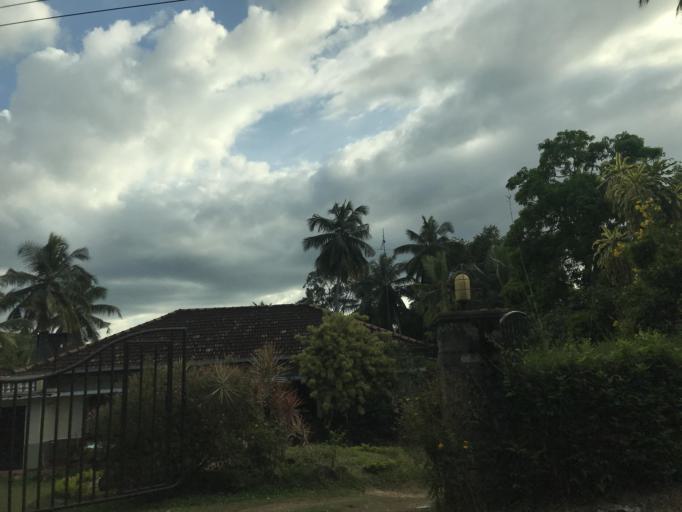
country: LK
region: Western
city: Gampaha
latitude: 7.0788
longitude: 79.9884
